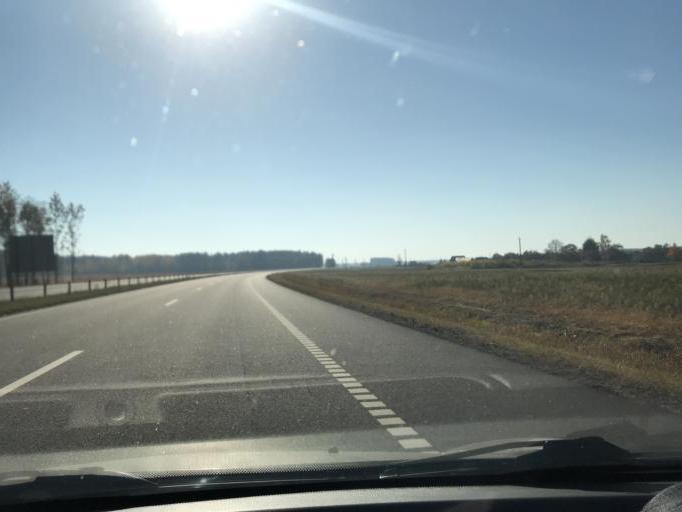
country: BY
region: Mogilev
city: Babruysk
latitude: 53.1359
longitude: 29.3661
